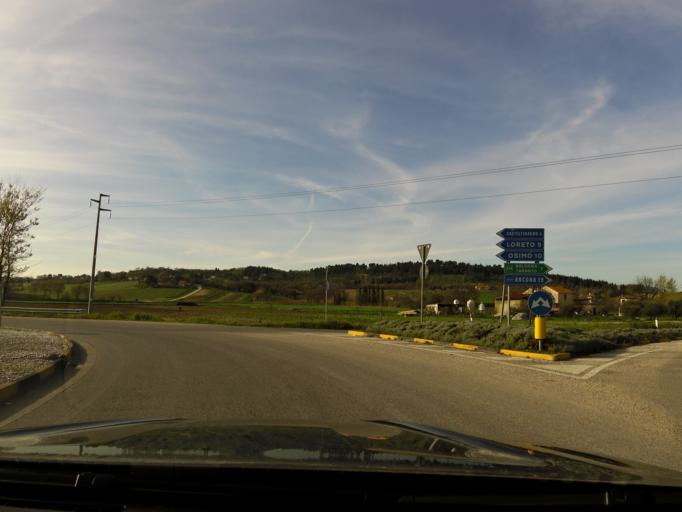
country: IT
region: The Marches
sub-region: Provincia di Ancona
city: Villa Musone
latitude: 43.4556
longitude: 13.5957
